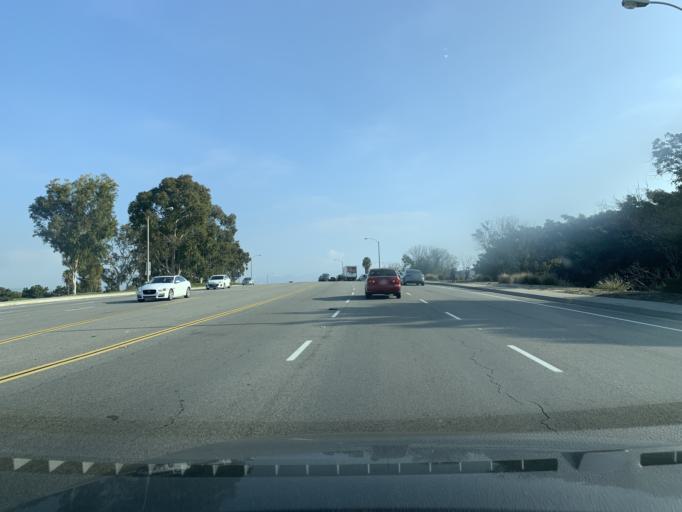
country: US
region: California
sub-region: Orange County
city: Lake Forest
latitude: 33.6482
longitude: -117.7241
